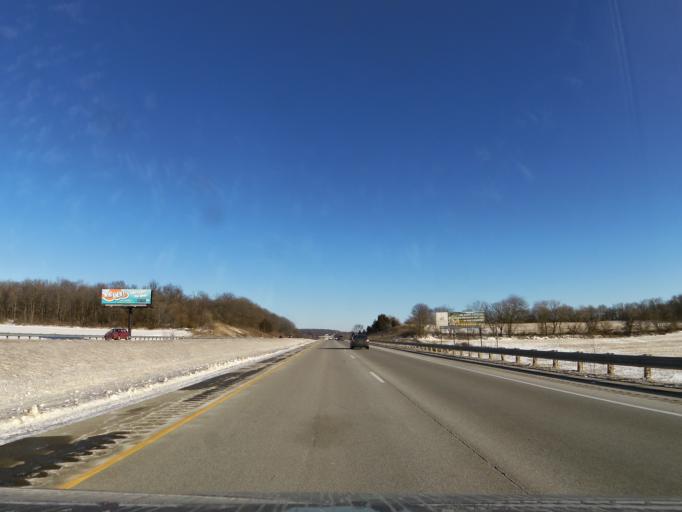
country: US
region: Wisconsin
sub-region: Jefferson County
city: Waterloo
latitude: 43.1107
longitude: -89.0054
